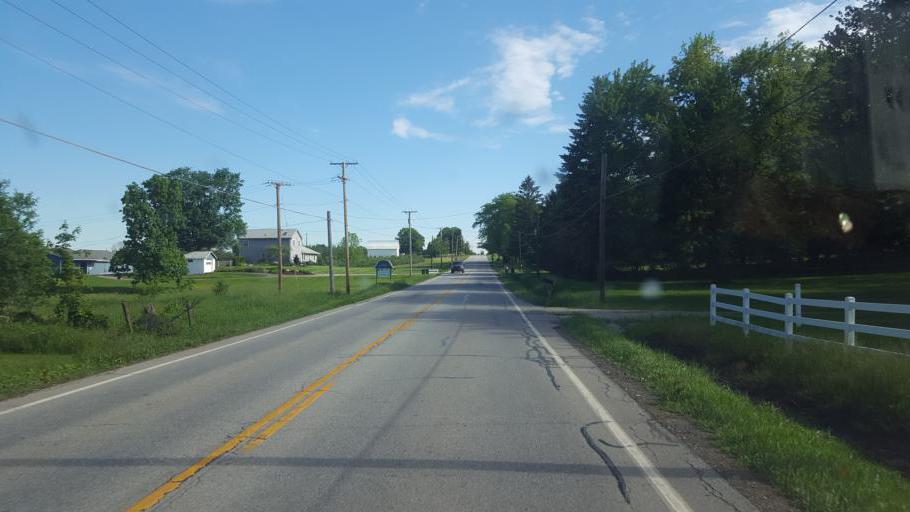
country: US
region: Ohio
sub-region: Medina County
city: Seville
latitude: 41.0413
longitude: -81.8644
